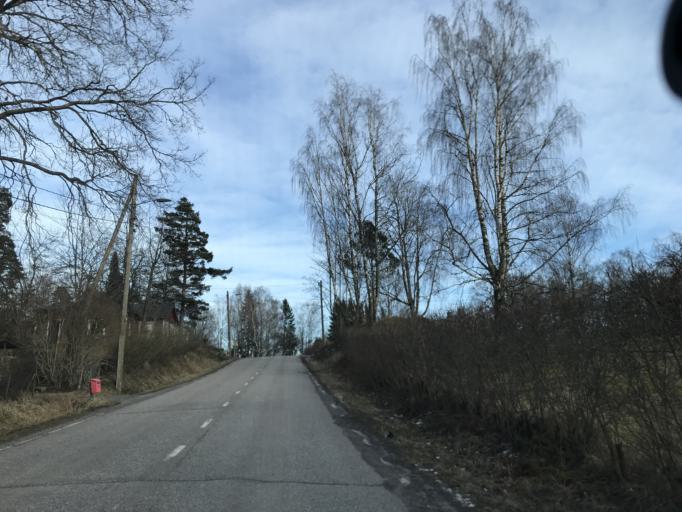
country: FI
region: Uusimaa
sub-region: Raaseporin
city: Pohja
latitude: 60.0961
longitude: 23.5308
